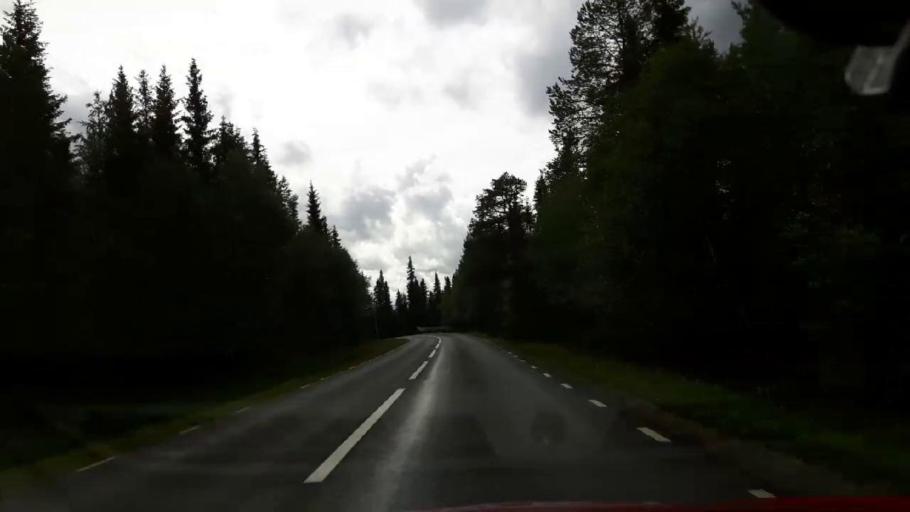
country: NO
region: Nord-Trondelag
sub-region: Lierne
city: Sandvika
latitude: 64.5124
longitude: 14.1562
